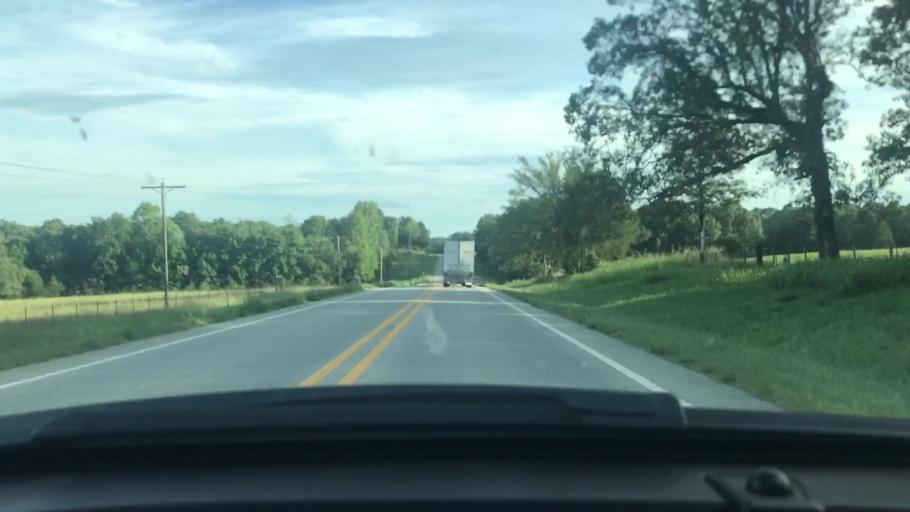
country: US
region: Arkansas
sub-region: Lawrence County
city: Hoxie
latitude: 36.1593
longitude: -91.1620
